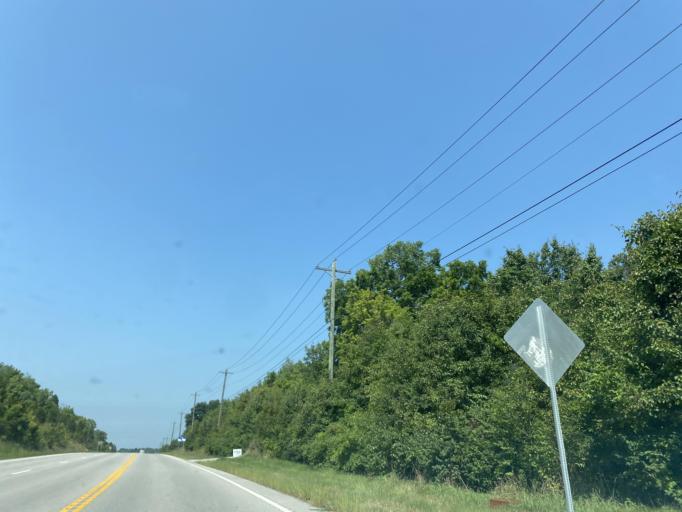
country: US
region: Kentucky
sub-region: Campbell County
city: Claryville
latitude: 38.9404
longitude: -84.3979
